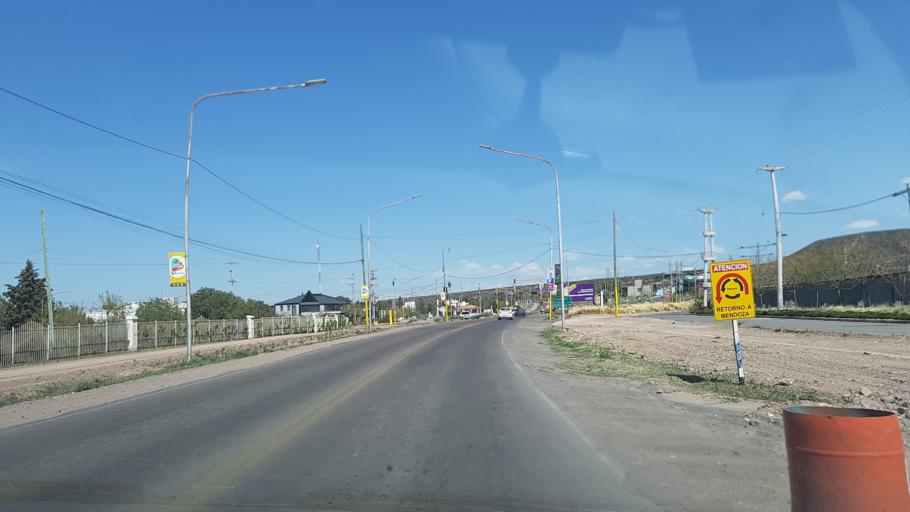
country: AR
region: Mendoza
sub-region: Departamento de Godoy Cruz
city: Godoy Cruz
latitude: -32.9677
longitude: -68.8756
